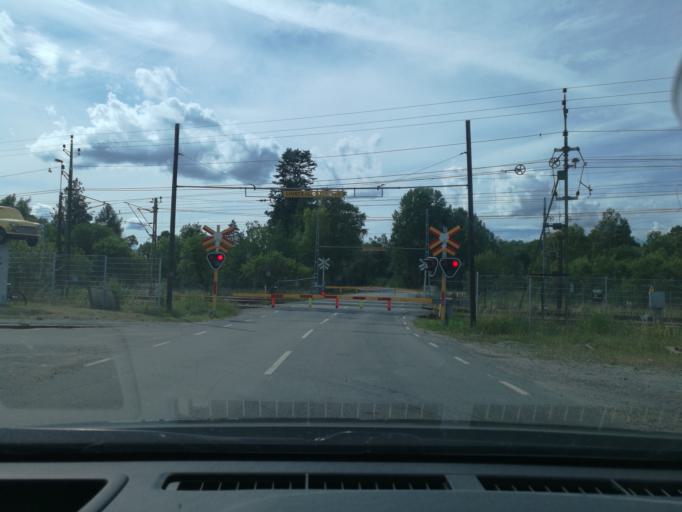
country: SE
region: Stockholm
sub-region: Sigtuna Kommun
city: Rosersberg
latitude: 59.5866
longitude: 17.8792
